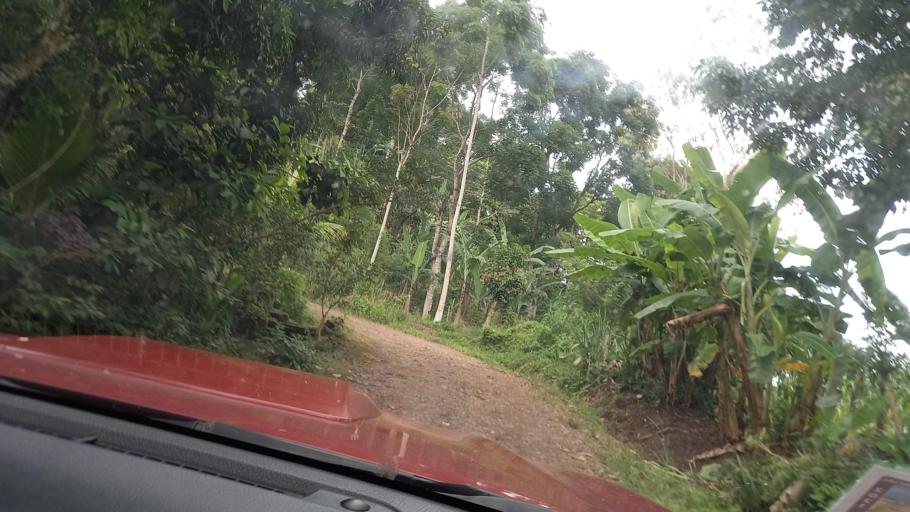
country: NI
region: Jinotega
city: San Jose de Bocay
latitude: 13.3391
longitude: -85.6576
